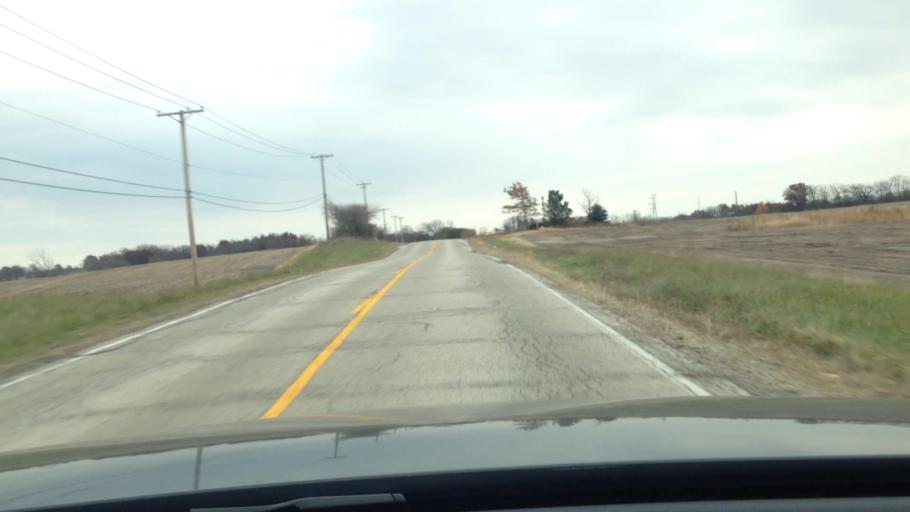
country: US
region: Illinois
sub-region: McHenry County
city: Woodstock
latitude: 42.2728
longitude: -88.4455
